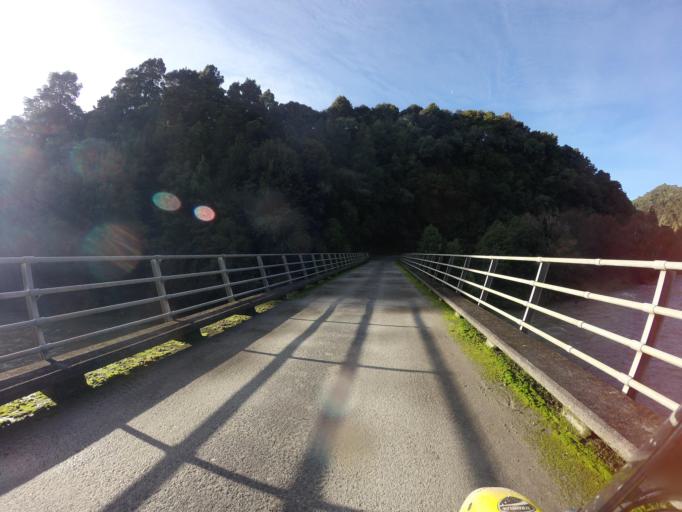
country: NZ
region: Hawke's Bay
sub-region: Wairoa District
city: Wairoa
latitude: -38.7477
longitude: 177.5185
